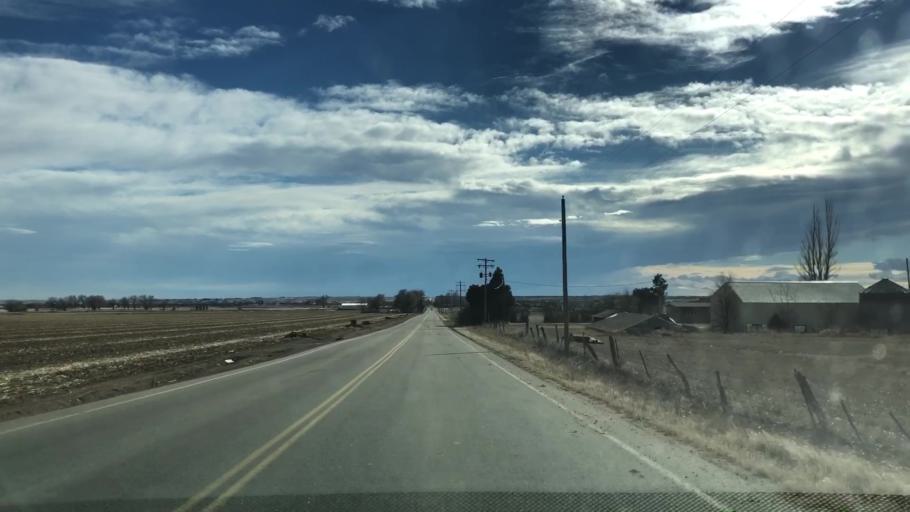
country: US
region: Colorado
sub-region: Weld County
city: Windsor
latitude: 40.5191
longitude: -104.9443
